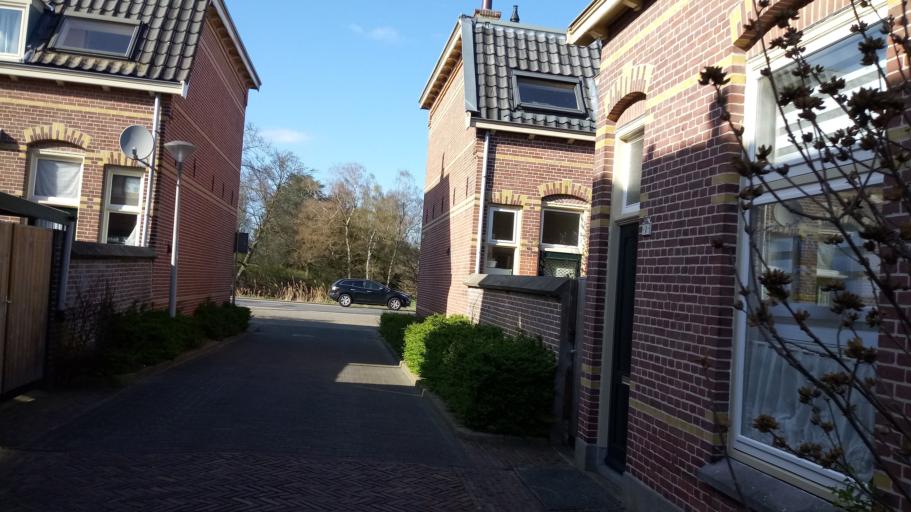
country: NL
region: Gelderland
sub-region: Gemeente Zutphen
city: Zutphen
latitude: 52.1415
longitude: 6.2118
